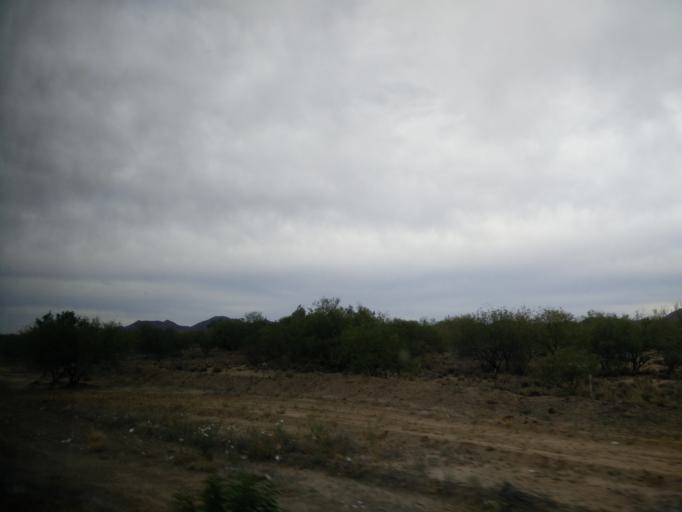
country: MX
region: Sonora
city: Hermosillo
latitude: 28.7391
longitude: -110.9760
